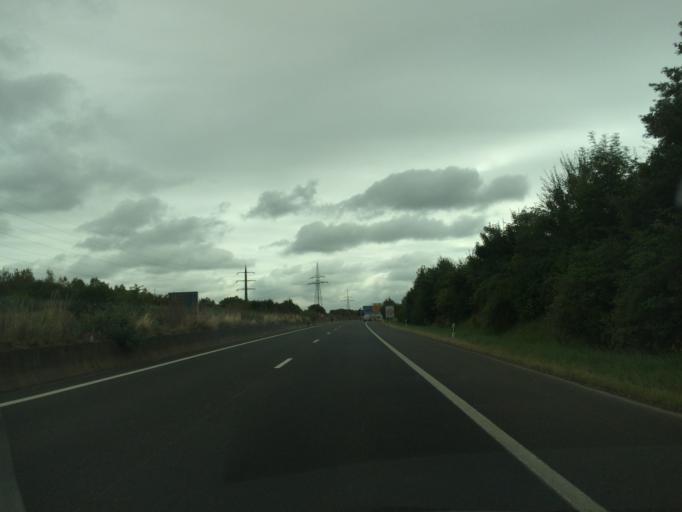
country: LU
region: Luxembourg
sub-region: Canton d'Esch-sur-Alzette
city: Dudelange
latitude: 49.5002
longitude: 6.0761
